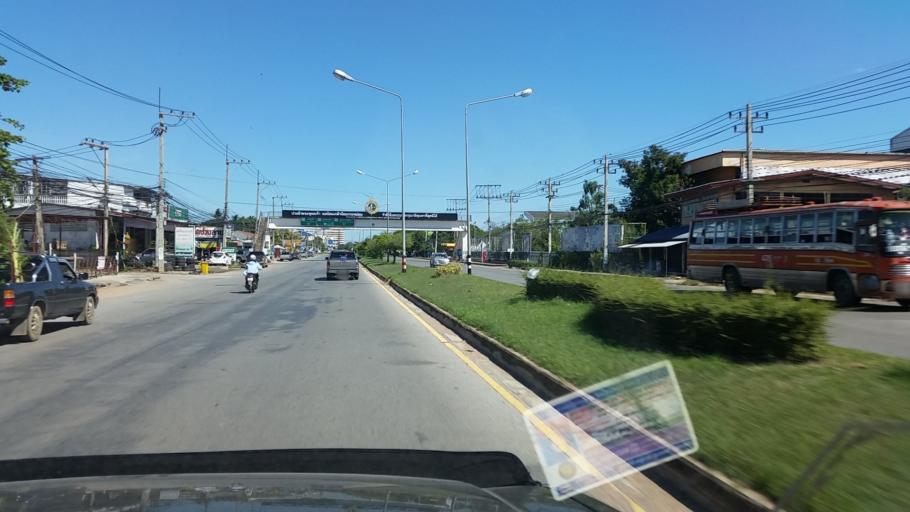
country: TH
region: Chaiyaphum
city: Chaiyaphum
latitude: 15.7971
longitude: 102.0234
